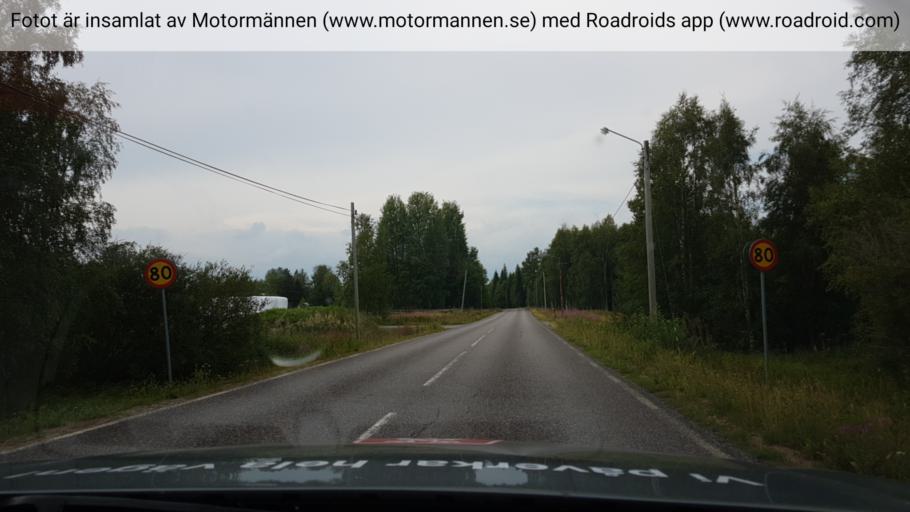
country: SE
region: Jaemtland
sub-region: Ragunda Kommun
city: Hammarstrand
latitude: 63.0089
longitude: 16.0672
